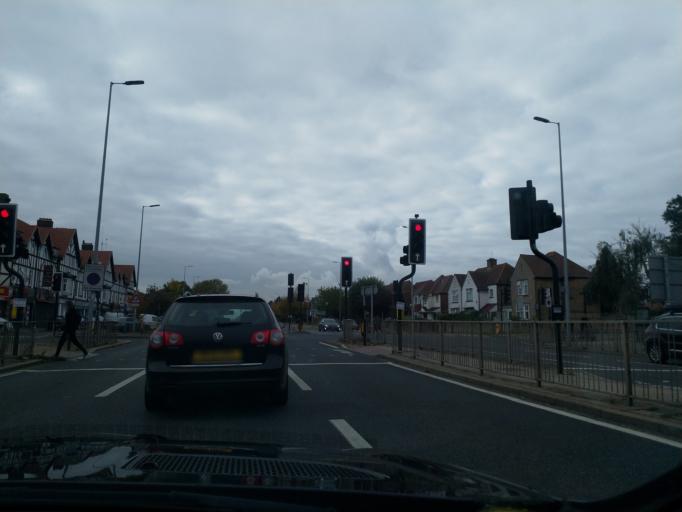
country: GB
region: England
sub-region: Greater London
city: Hounslow
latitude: 51.4790
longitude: -0.3639
